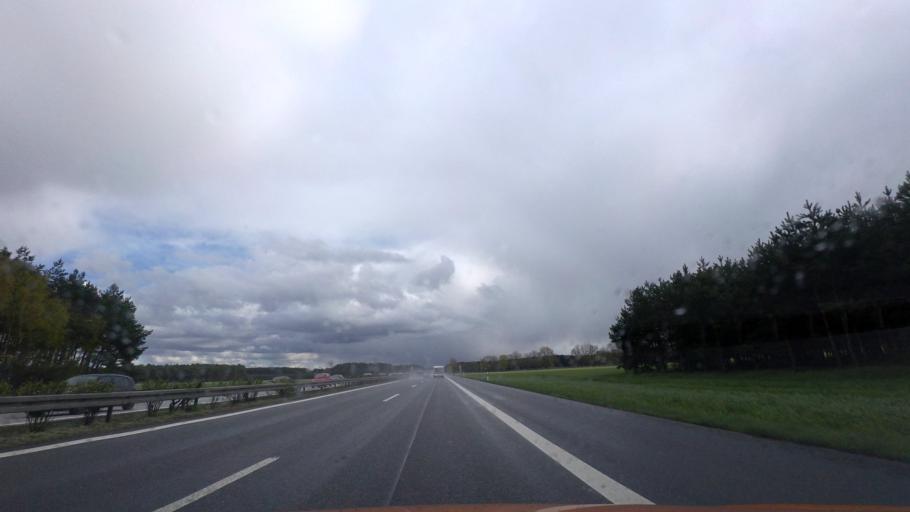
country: DE
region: Mecklenburg-Vorpommern
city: Sulstorf
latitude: 53.4532
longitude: 11.3588
